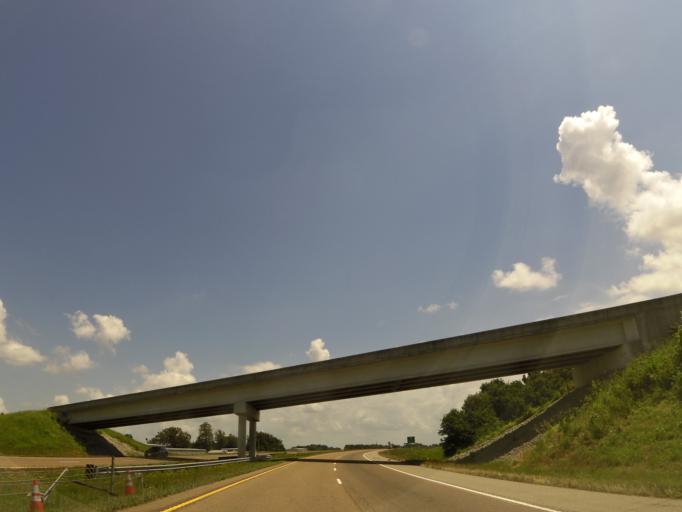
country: US
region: Tennessee
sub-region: Crockett County
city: Alamo
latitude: 35.8127
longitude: -89.1613
